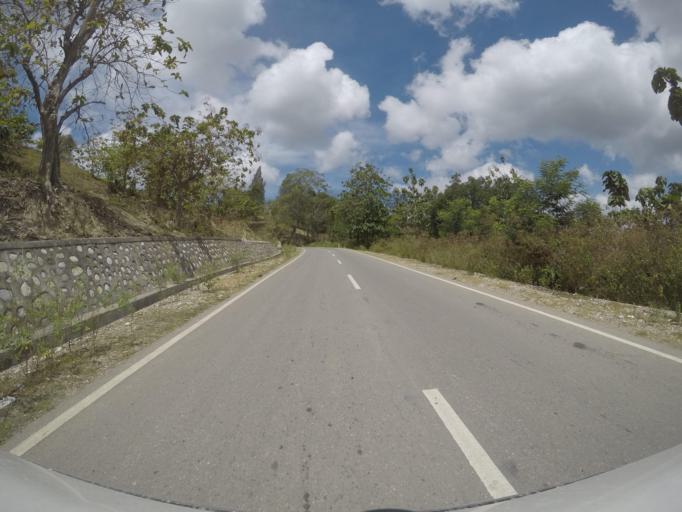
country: TL
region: Viqueque
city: Viqueque
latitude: -8.8750
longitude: 126.3761
